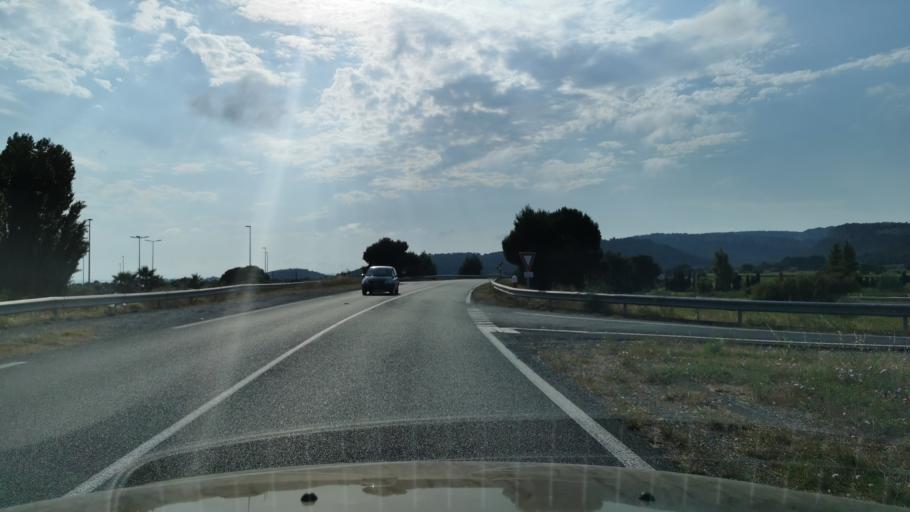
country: FR
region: Languedoc-Roussillon
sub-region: Departement de l'Aude
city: Gruissan
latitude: 43.1181
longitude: 3.1067
